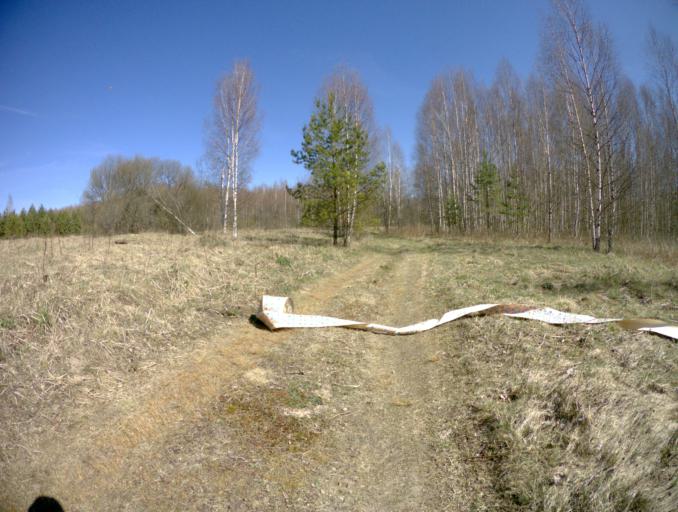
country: RU
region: Vladimir
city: Ivanishchi
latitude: 55.8620
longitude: 40.4151
